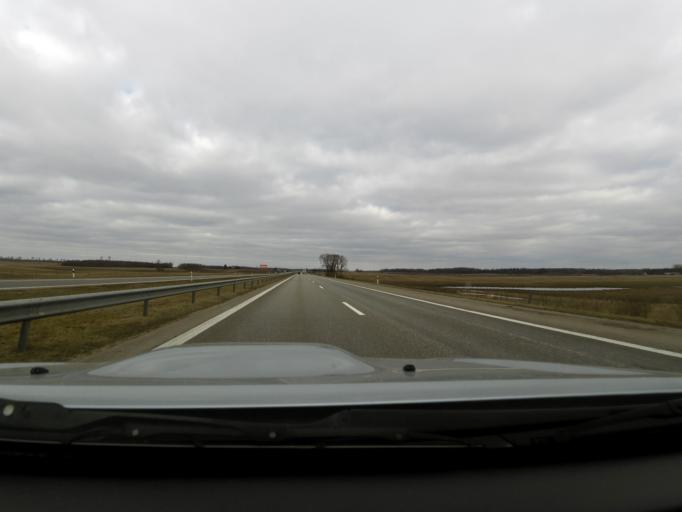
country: LT
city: Sirvintos
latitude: 55.1340
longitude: 24.8346
